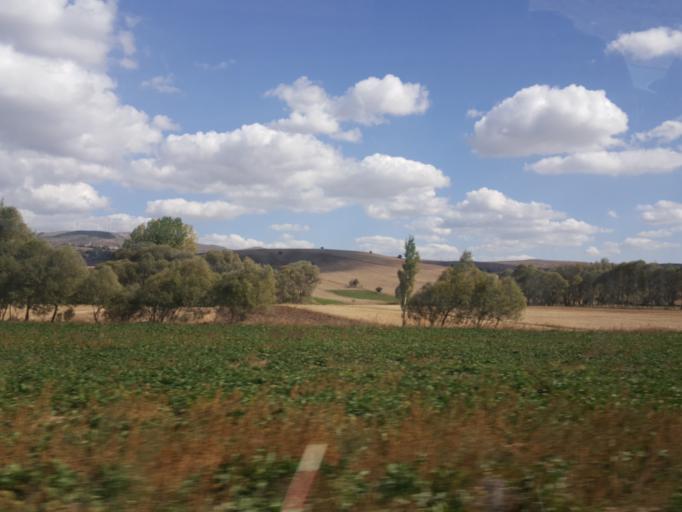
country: TR
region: Tokat
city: Camlibel
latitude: 40.1902
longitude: 36.4565
